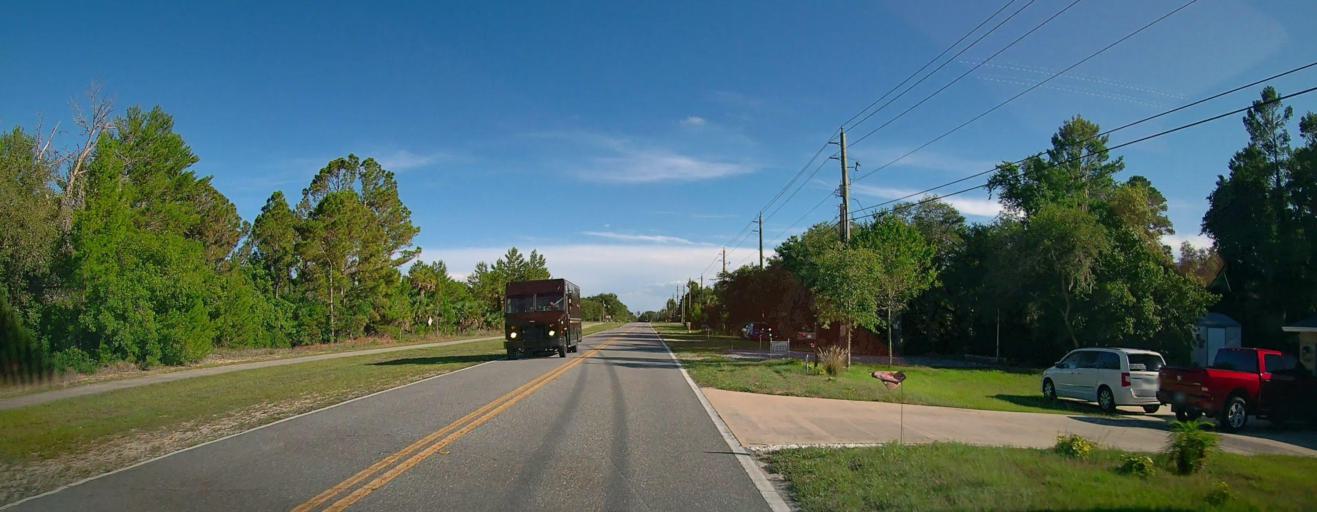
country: US
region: Florida
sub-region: Brevard County
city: Titusville
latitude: 28.5502
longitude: -80.8226
